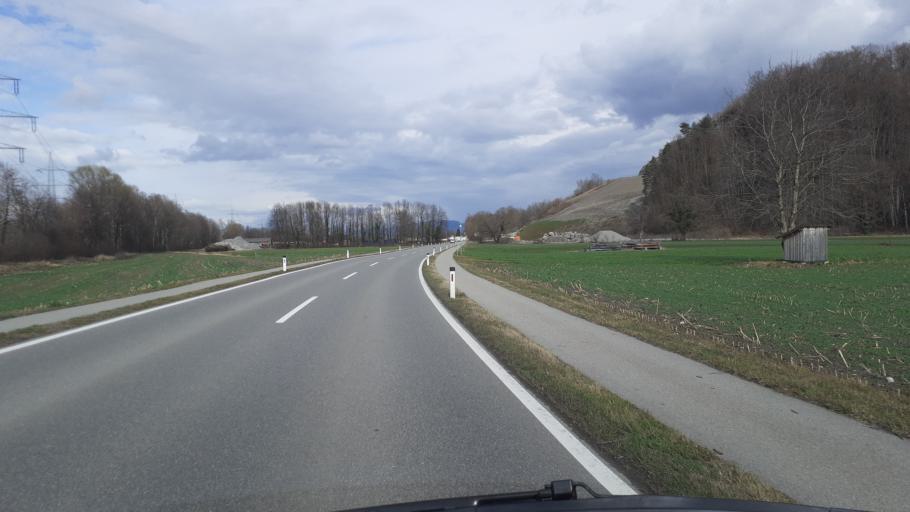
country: AT
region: Vorarlberg
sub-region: Politischer Bezirk Feldkirch
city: Koblach
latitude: 47.3384
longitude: 9.5991
